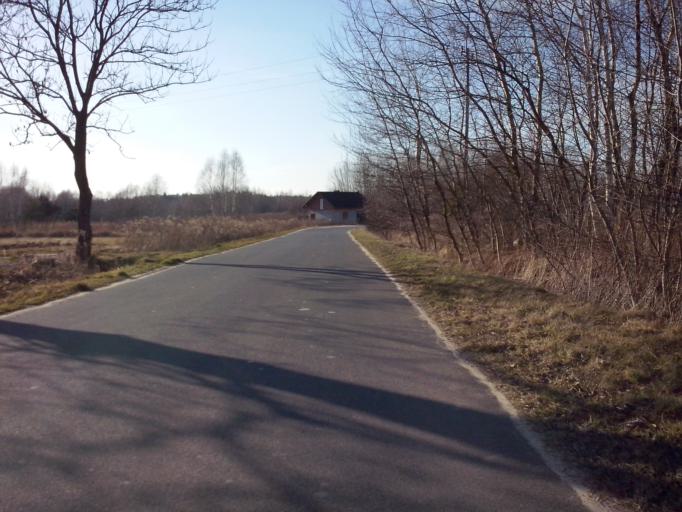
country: PL
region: Subcarpathian Voivodeship
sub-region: Powiat nizanski
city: Krzeszow
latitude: 50.4121
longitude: 22.3524
